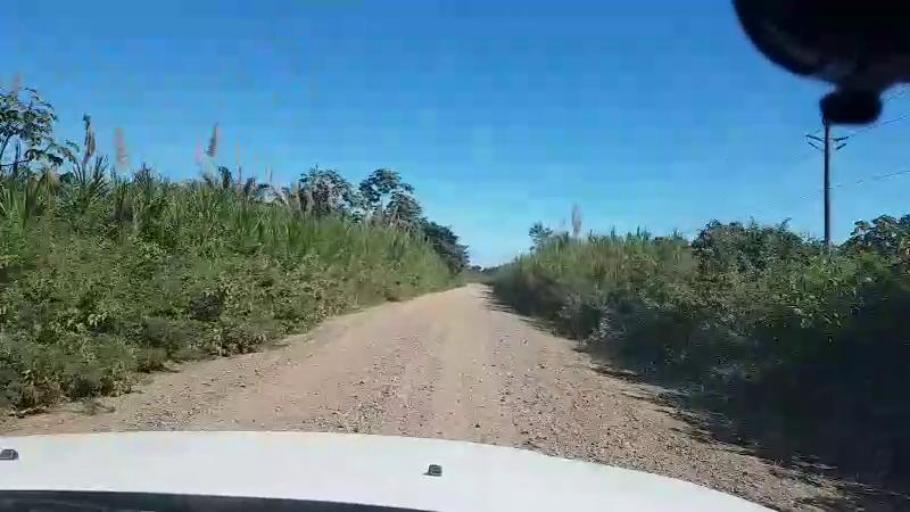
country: BZ
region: Stann Creek
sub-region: Dangriga
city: Dangriga
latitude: 17.1583
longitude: -88.3340
